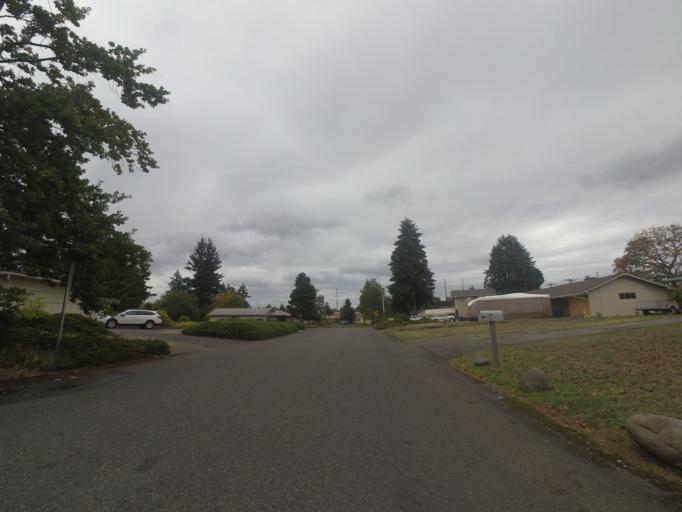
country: US
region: Washington
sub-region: Pierce County
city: McChord Air Force Base
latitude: 47.1500
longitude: -122.5074
